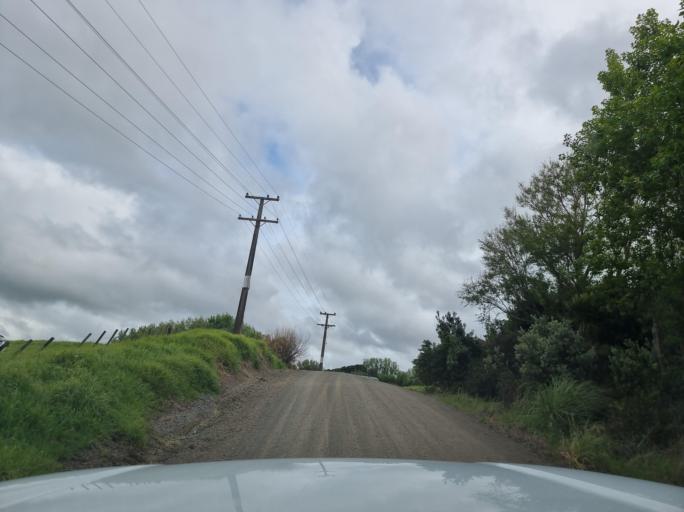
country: NZ
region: Northland
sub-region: Whangarei
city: Ruakaka
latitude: -36.1286
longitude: 174.2083
